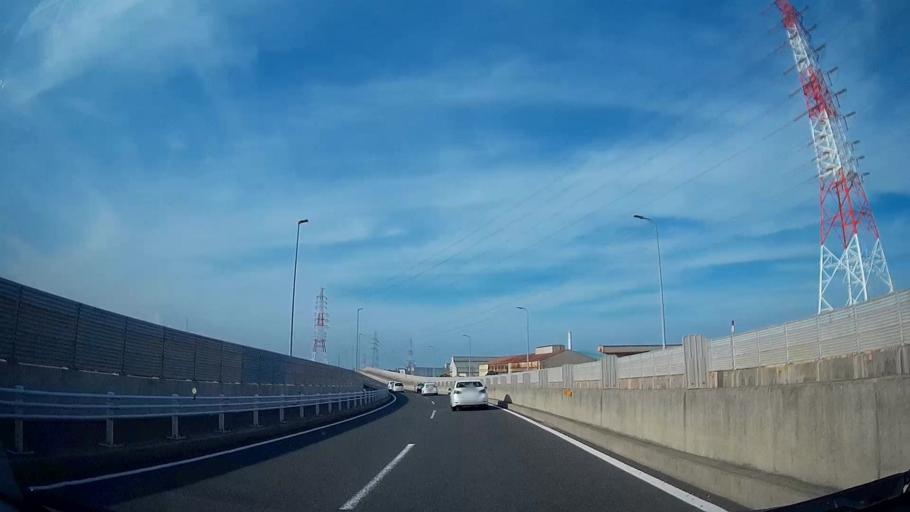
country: JP
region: Aichi
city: Handa
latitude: 34.8676
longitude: 136.9285
